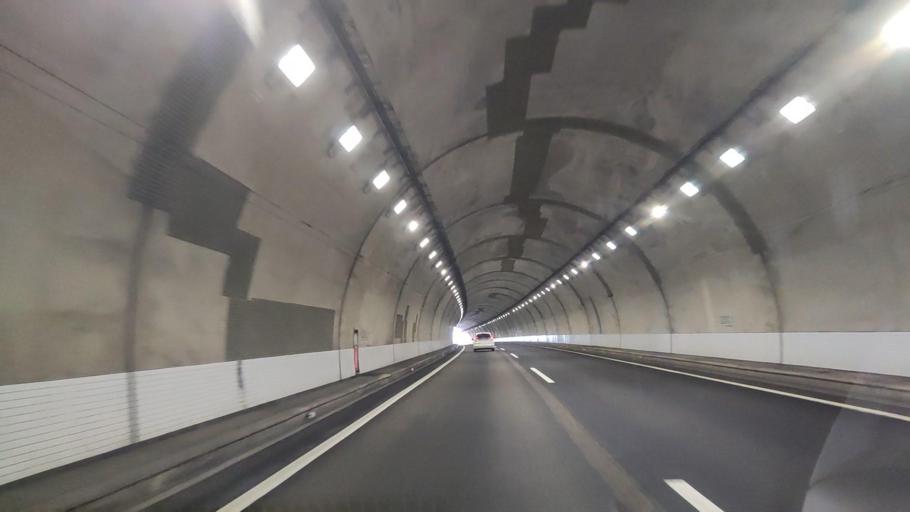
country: JP
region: Niigata
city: Joetsu
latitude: 37.1048
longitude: 138.2202
